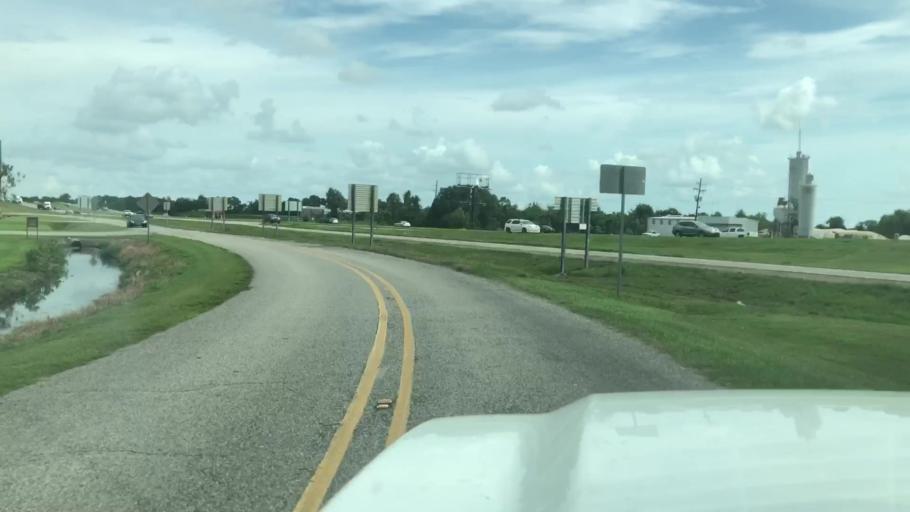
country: US
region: Louisiana
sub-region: Iberia Parish
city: New Iberia
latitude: 29.9843
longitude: -91.8571
